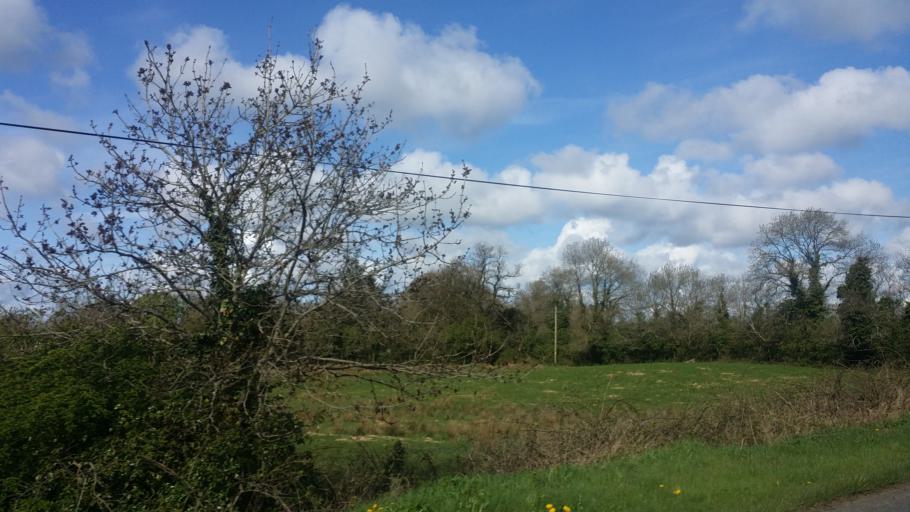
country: IE
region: Ulster
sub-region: An Cabhan
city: Virginia
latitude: 53.7929
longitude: -7.0262
